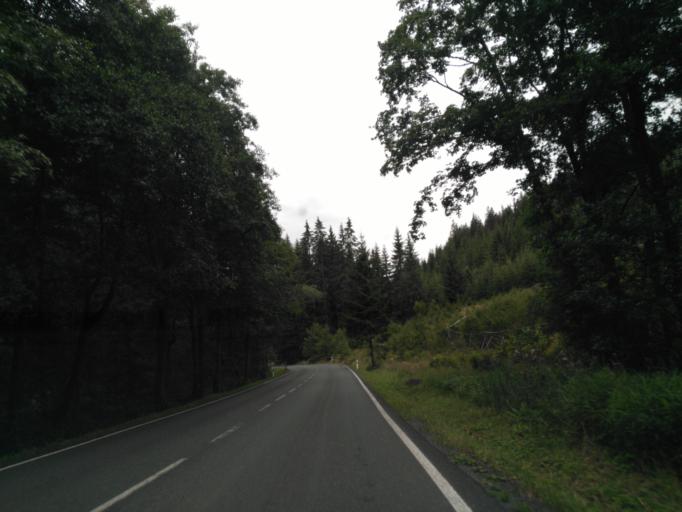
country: DE
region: Saxony
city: Johanngeorgenstadt
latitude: 50.4055
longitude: 12.7401
